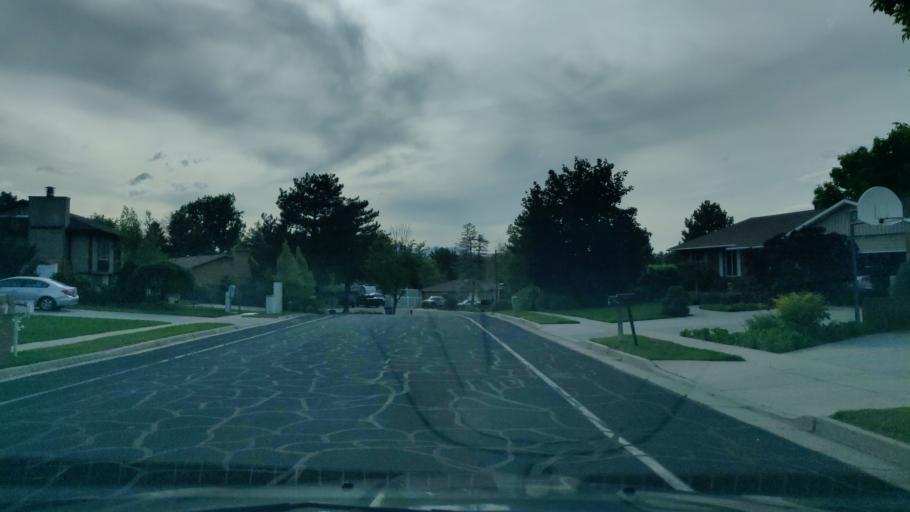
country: US
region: Utah
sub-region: Salt Lake County
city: Little Cottonwood Creek Valley
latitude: 40.6171
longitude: -111.8450
